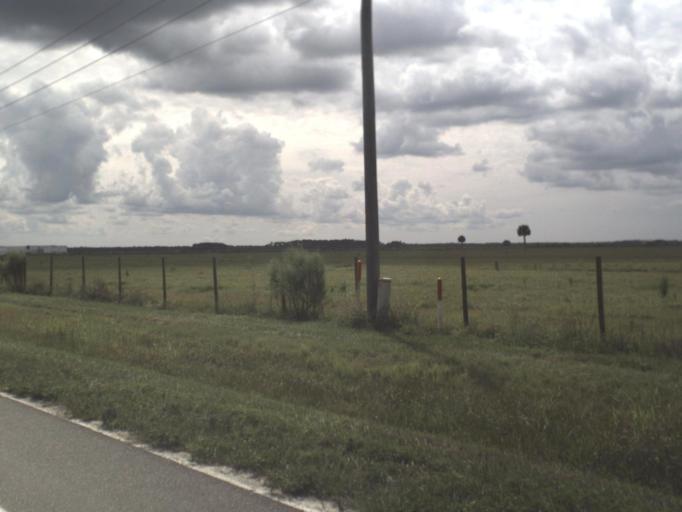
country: US
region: Florida
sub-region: DeSoto County
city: Nocatee
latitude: 27.0034
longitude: -81.7605
